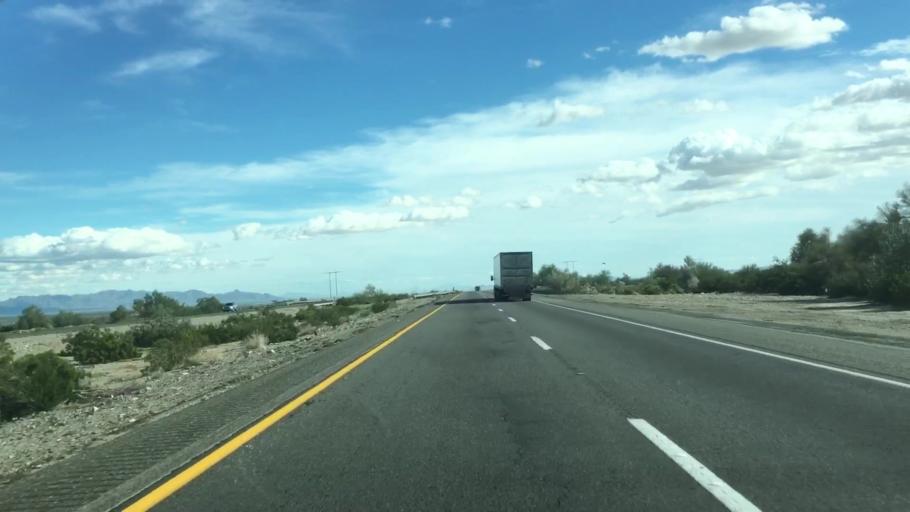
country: US
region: California
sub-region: Riverside County
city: Mesa Verde
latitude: 33.6780
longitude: -115.2292
